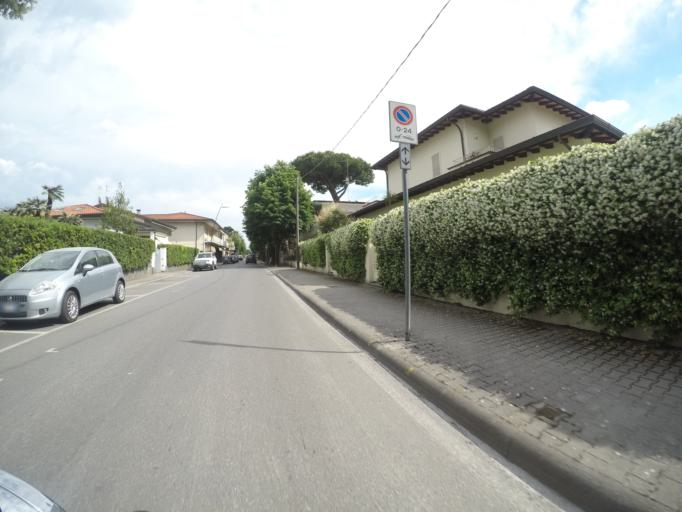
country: IT
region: Tuscany
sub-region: Provincia di Lucca
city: Forte dei Marmi
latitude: 43.9705
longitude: 10.1556
